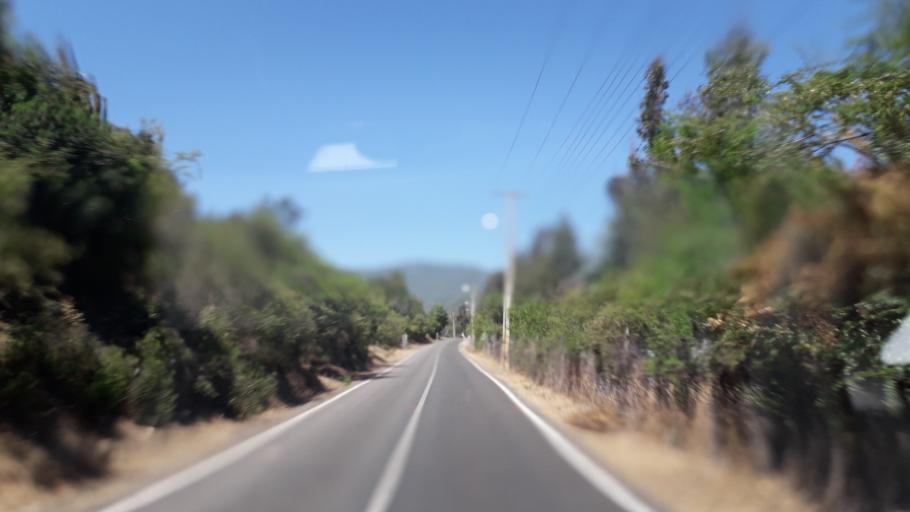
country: CL
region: Valparaiso
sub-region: Provincia de Marga Marga
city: Limache
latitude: -33.0809
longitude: -71.2118
